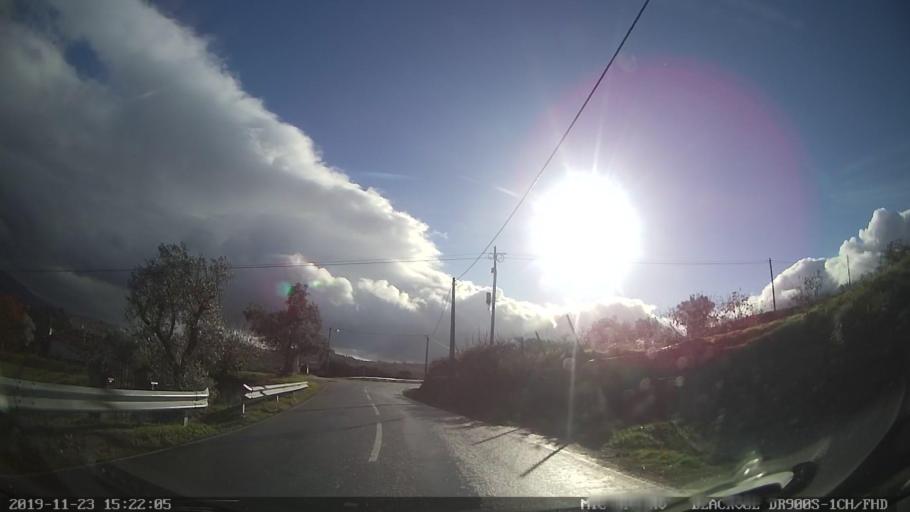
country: PT
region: Viseu
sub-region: Lamego
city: Lamego
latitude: 41.1074
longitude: -7.7922
